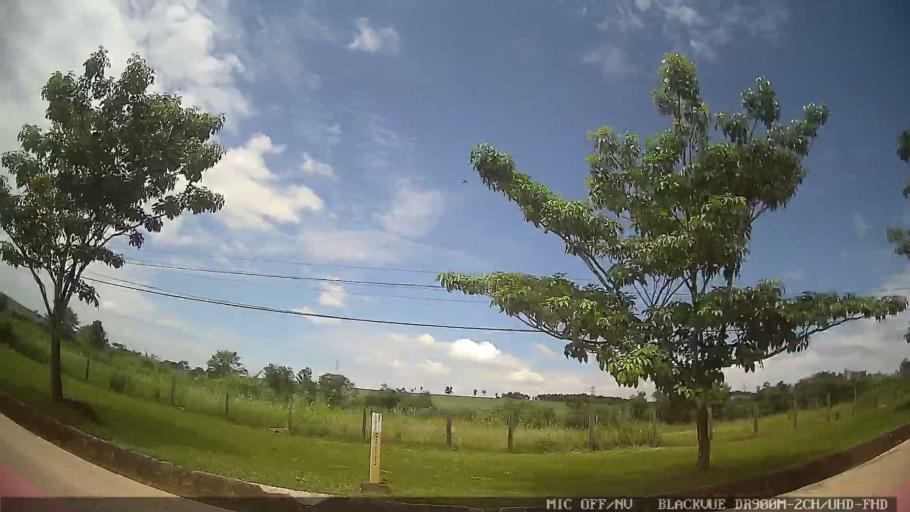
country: BR
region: Sao Paulo
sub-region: Laranjal Paulista
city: Laranjal Paulista
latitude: -23.0676
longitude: -47.8241
